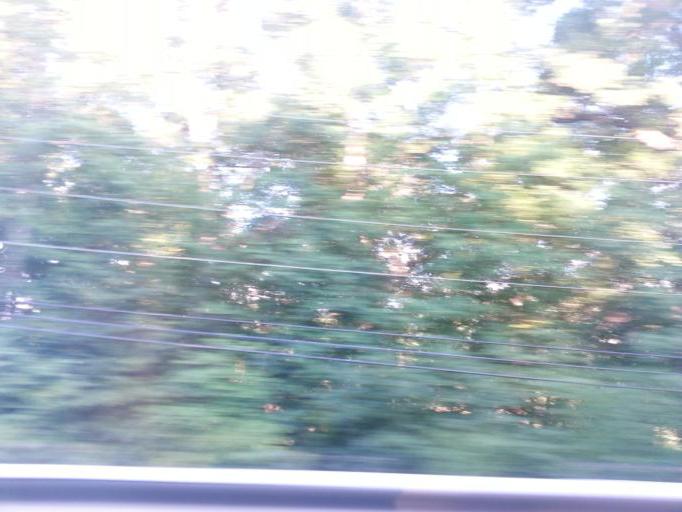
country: US
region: Tennessee
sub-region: Anderson County
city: Oak Ridge
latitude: 36.0113
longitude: -84.1744
